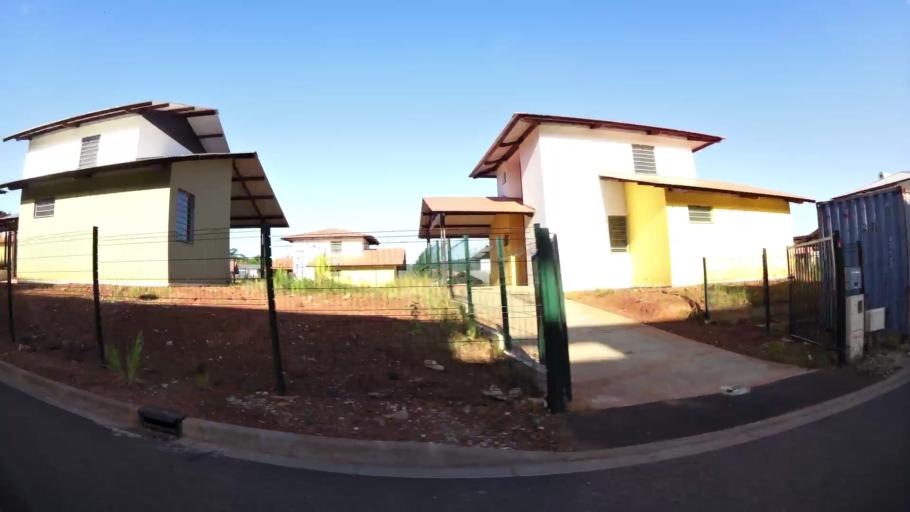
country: GF
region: Guyane
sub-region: Guyane
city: Remire-Montjoly
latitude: 4.8865
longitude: -52.2983
